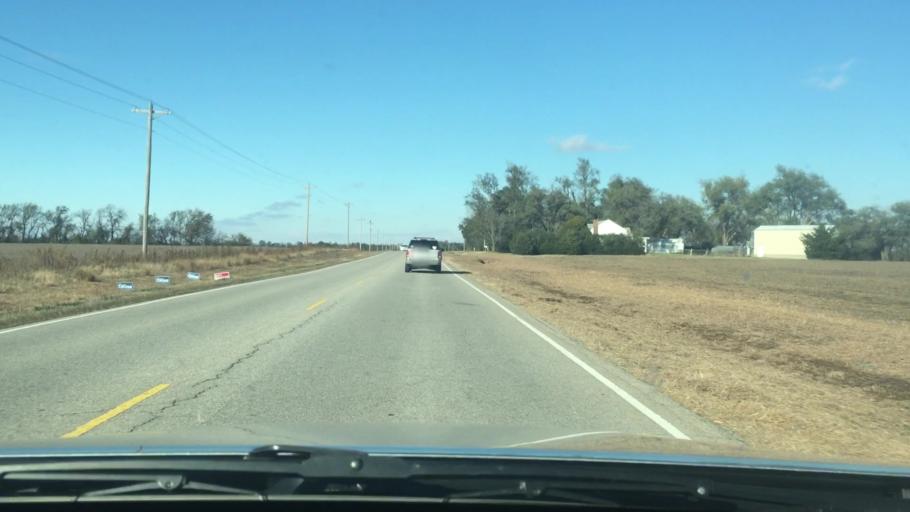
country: US
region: Kansas
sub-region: Sedgwick County
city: Maize
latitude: 37.7489
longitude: -97.4809
